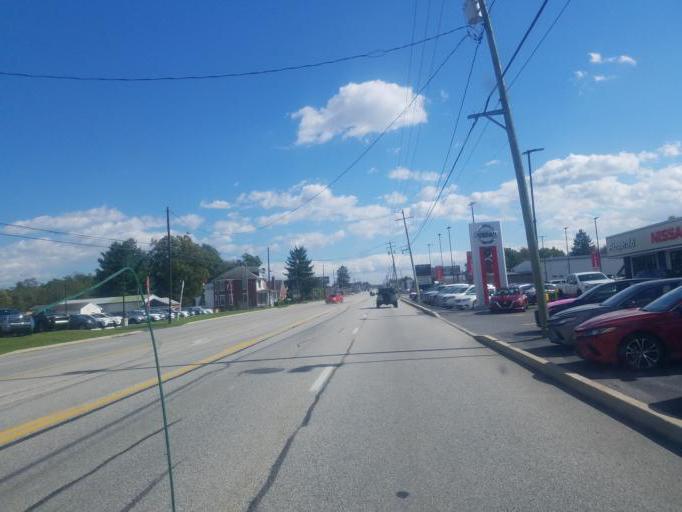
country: US
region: Pennsylvania
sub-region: Franklin County
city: Guilford
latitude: 39.9257
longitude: -77.6202
